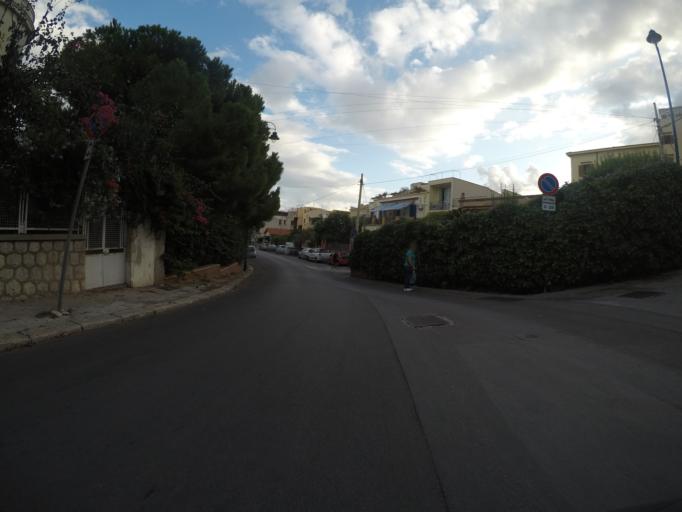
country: IT
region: Sicily
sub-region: Palermo
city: Palermo
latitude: 38.2095
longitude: 13.3271
